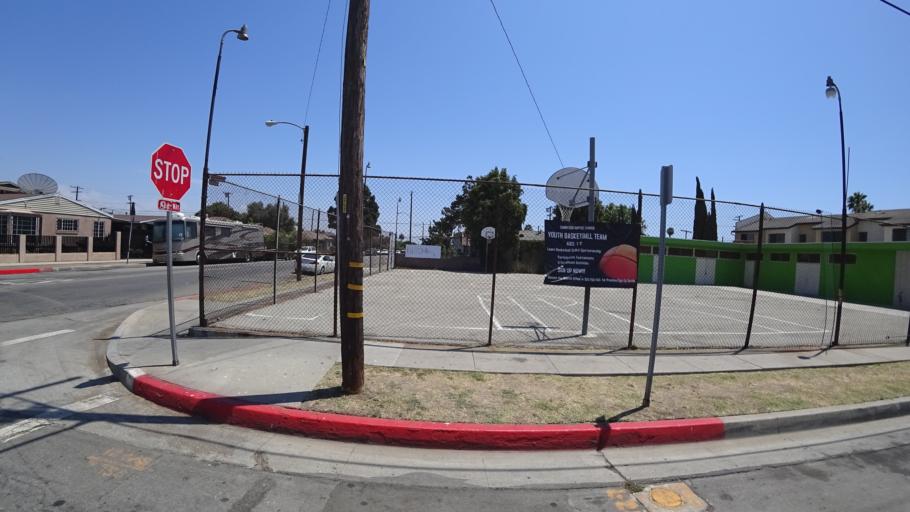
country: US
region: California
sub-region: Los Angeles County
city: Westmont
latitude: 33.9508
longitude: -118.2959
